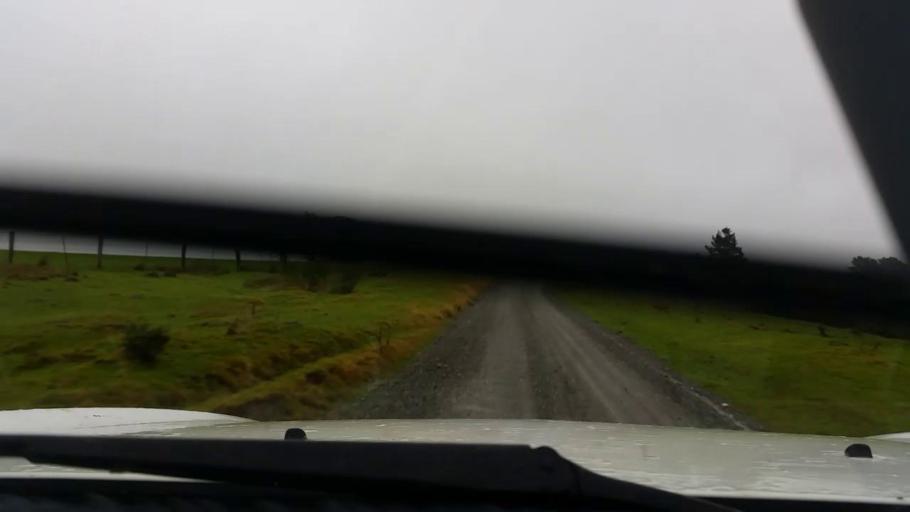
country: NZ
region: Wellington
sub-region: Masterton District
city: Masterton
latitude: -41.2504
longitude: 175.9006
